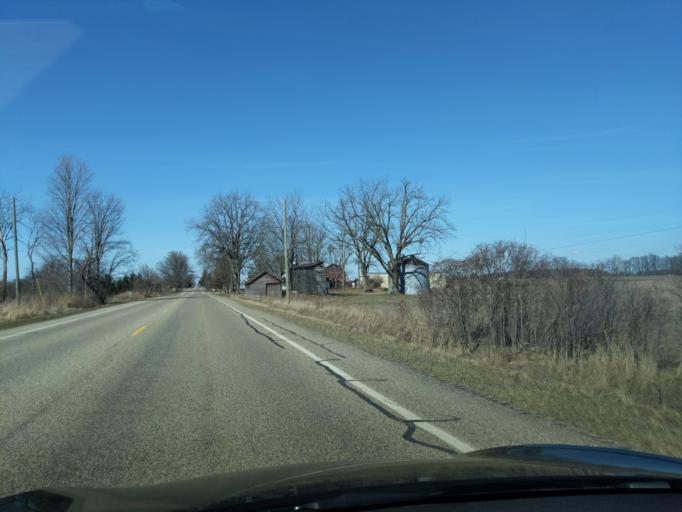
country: US
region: Michigan
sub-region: Ionia County
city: Lake Odessa
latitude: 42.8312
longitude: -85.1337
